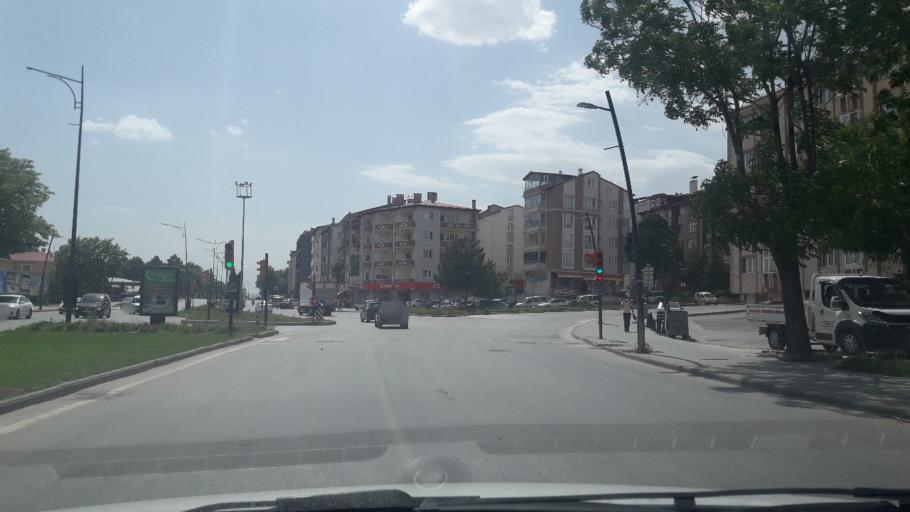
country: TR
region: Sivas
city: Sivas
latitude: 39.7355
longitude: 36.9937
